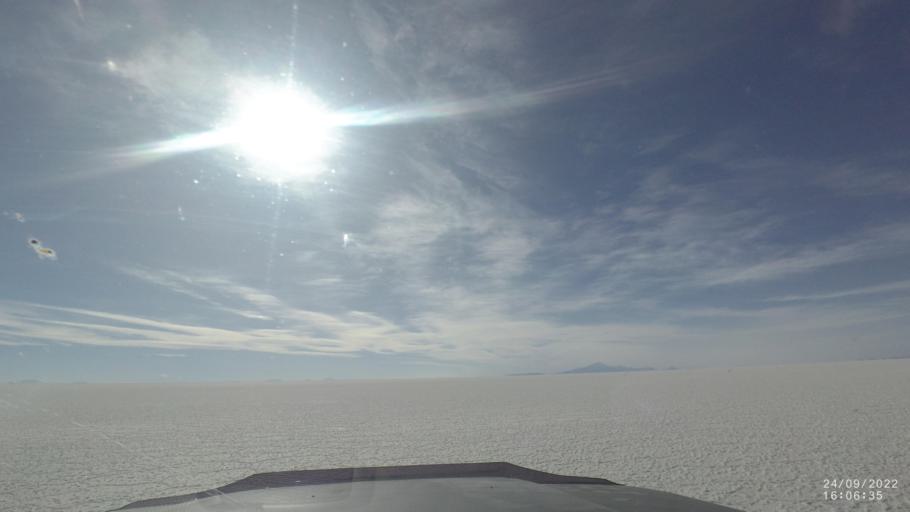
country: BO
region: Potosi
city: Colchani
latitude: -20.3049
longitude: -67.2954
